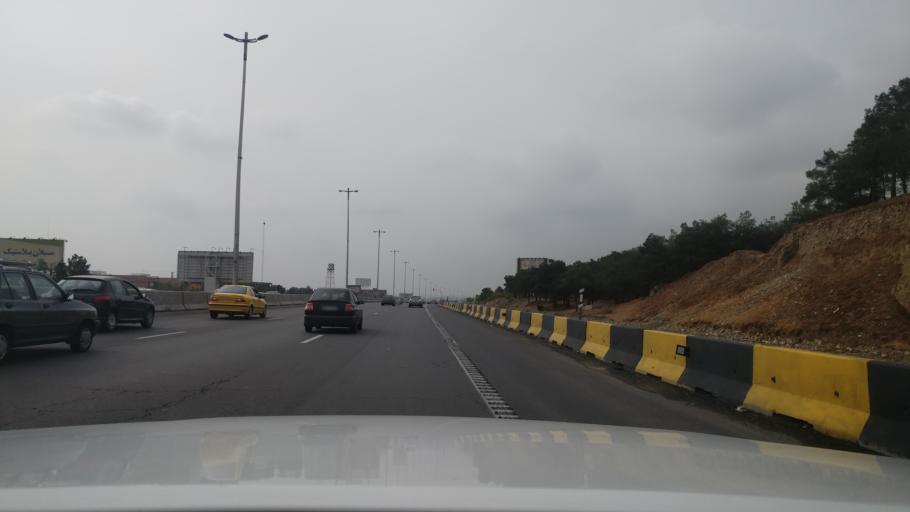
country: IR
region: Tehran
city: Shahr-e Qods
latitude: 35.7181
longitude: 51.2250
